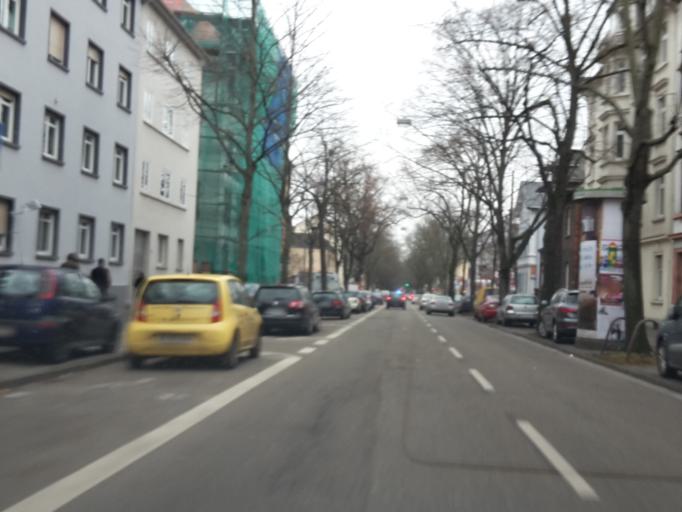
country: DE
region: Hesse
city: Sulzbach
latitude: 50.1091
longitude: 8.5403
